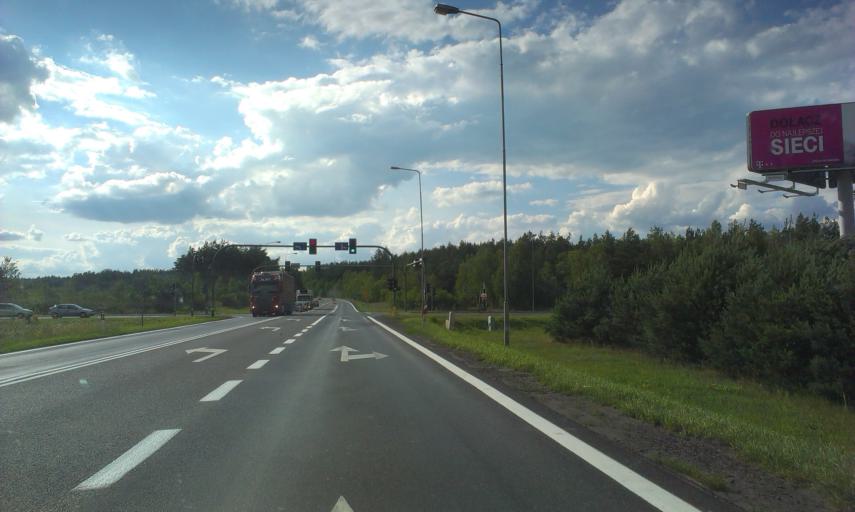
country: PL
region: Greater Poland Voivodeship
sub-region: Powiat pilski
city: Pila
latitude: 53.1862
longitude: 16.7626
